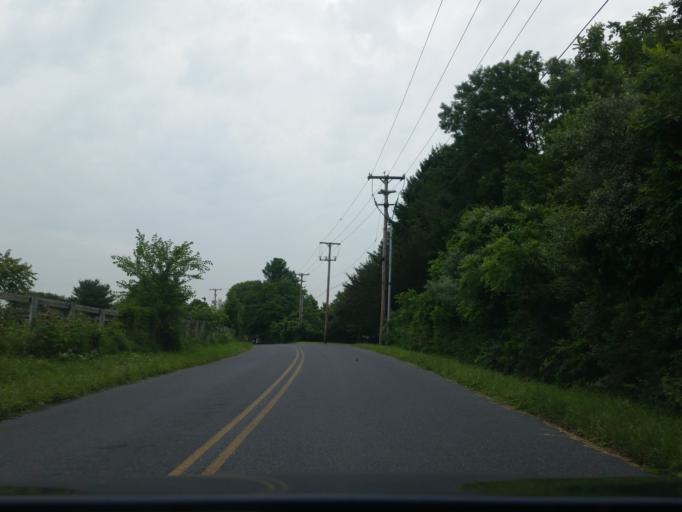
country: US
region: Pennsylvania
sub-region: Dauphin County
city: Skyline View
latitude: 40.4011
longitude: -76.6514
